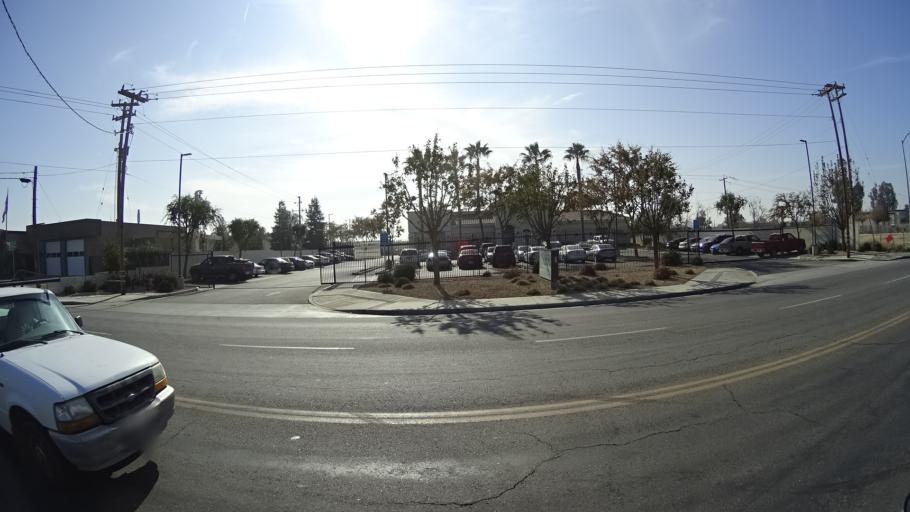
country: US
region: California
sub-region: Kern County
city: Bakersfield
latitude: 35.3538
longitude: -119.0054
